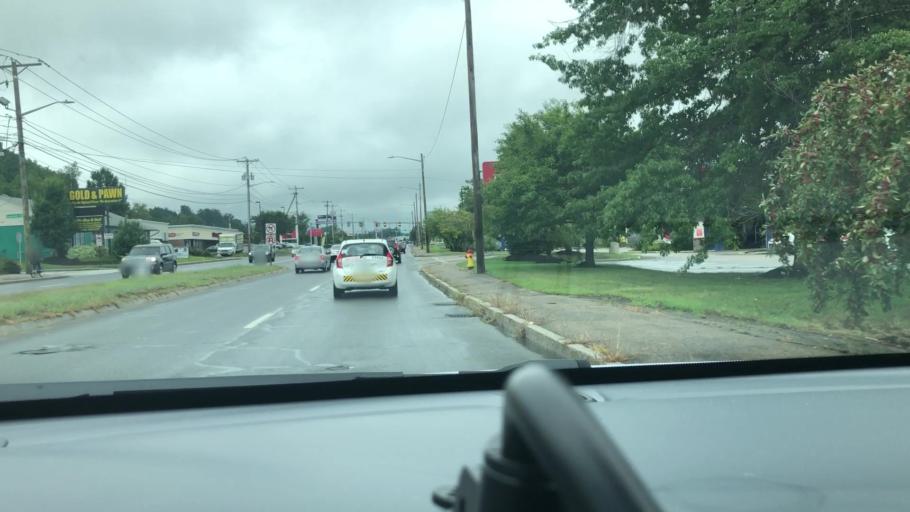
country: US
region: New Hampshire
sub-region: Hillsborough County
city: Manchester
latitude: 42.9638
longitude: -71.4439
